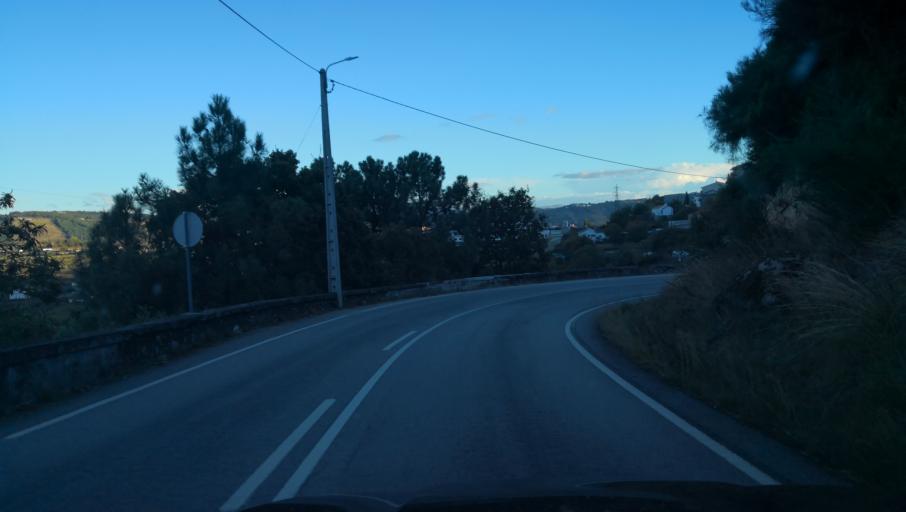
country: PT
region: Vila Real
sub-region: Vila Real
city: Vila Real
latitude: 41.2605
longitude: -7.7738
